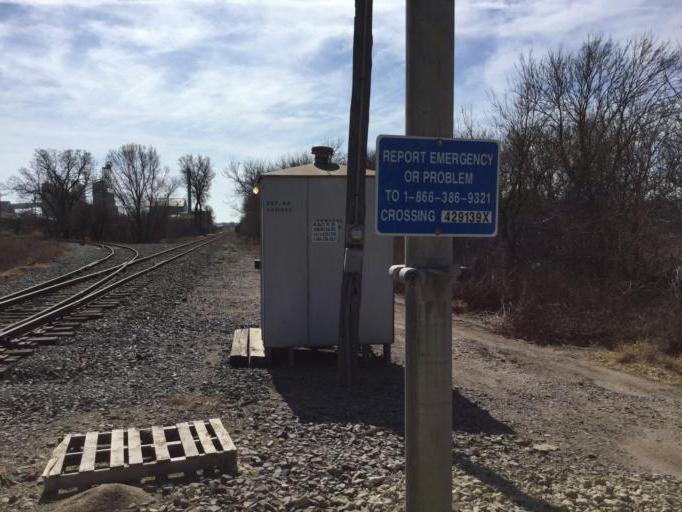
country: US
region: Kansas
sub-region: Rice County
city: Lyons
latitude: 38.3331
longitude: -98.1928
